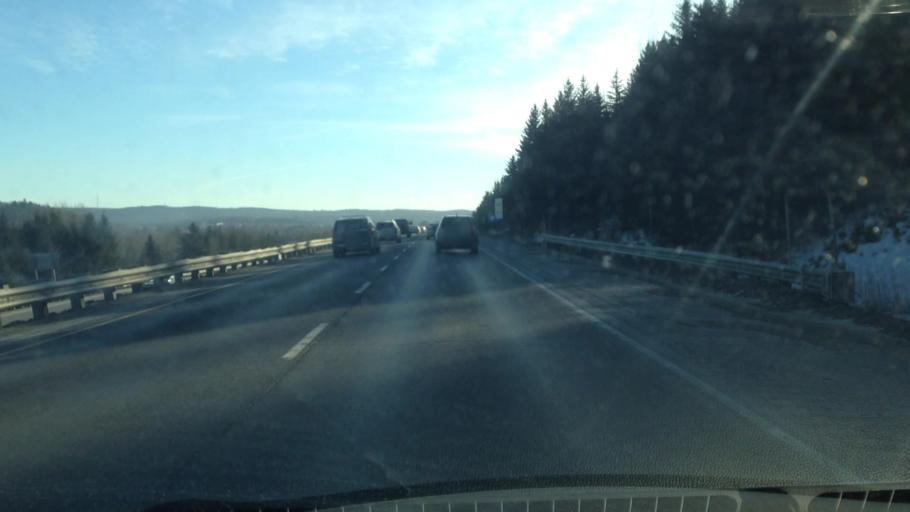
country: CA
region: Quebec
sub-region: Laurentides
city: Prevost
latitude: 45.8803
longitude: -74.0993
